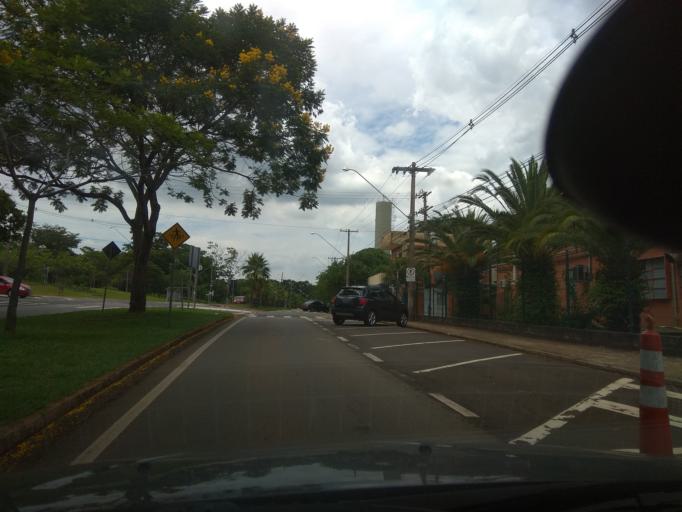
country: BR
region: Sao Paulo
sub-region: Campinas
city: Campinas
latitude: -22.8207
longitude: -47.0667
